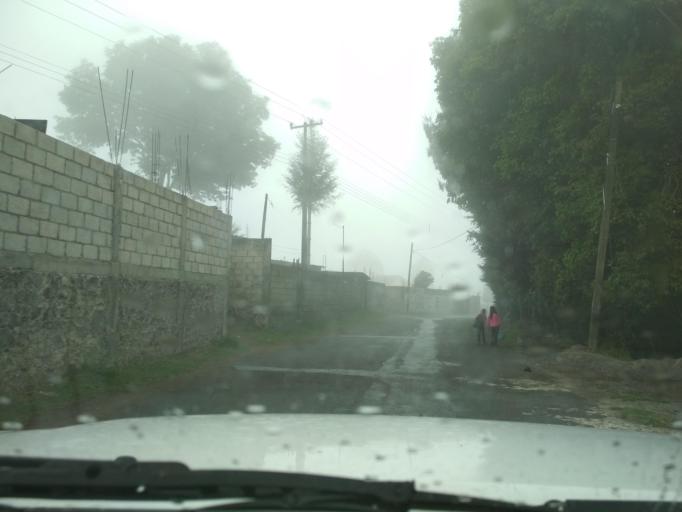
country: MX
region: Veracruz
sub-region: Mariano Escobedo
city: San Isidro el Berro
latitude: 18.9277
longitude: -97.2076
